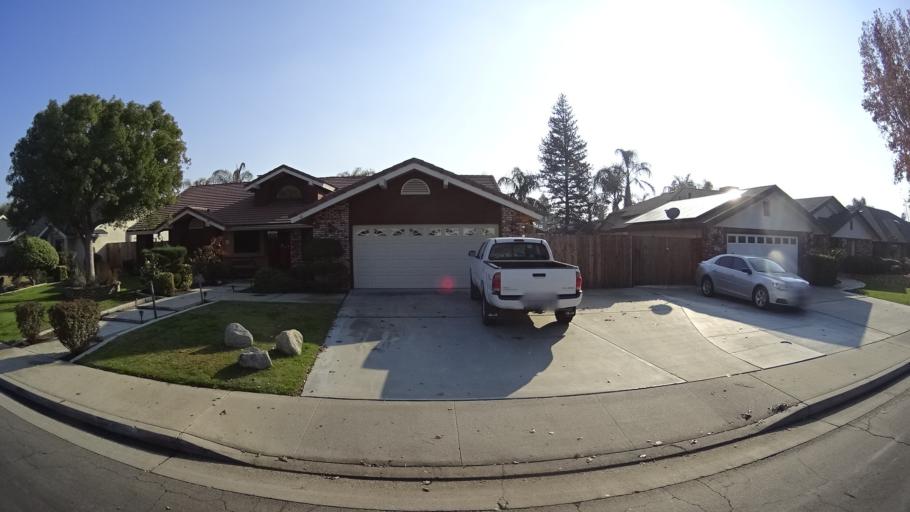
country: US
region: California
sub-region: Kern County
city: Greenacres
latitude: 35.3382
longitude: -119.1072
